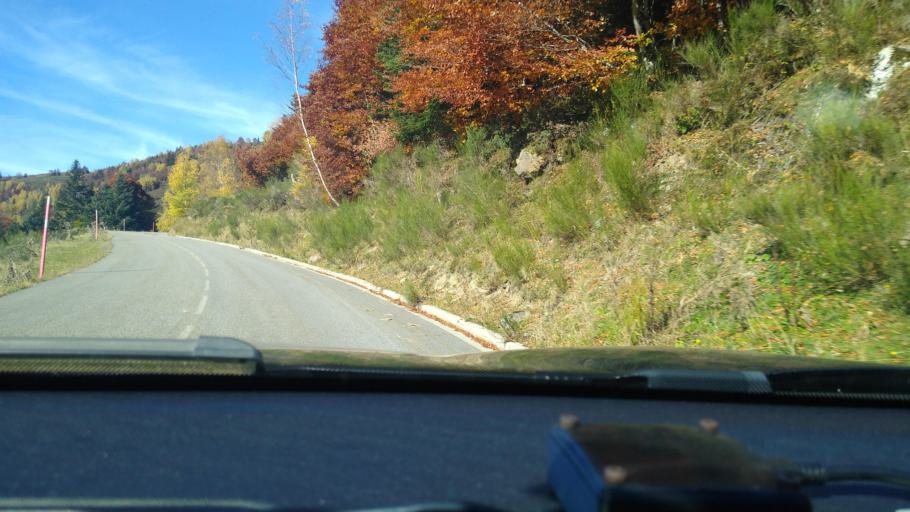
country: FR
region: Midi-Pyrenees
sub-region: Departement de l'Ariege
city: Ax-les-Thermes
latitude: 42.7281
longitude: 1.9594
